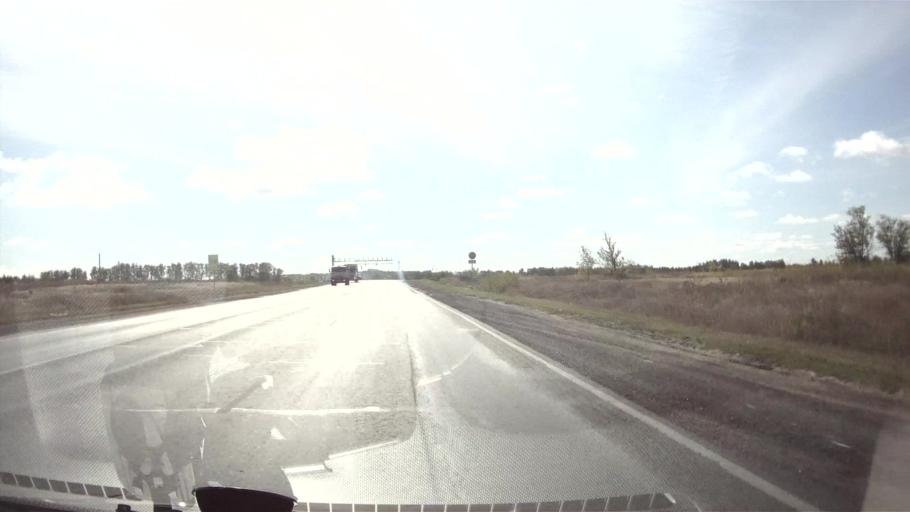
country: RU
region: Ulyanovsk
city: Isheyevka
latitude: 54.3003
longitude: 48.2454
